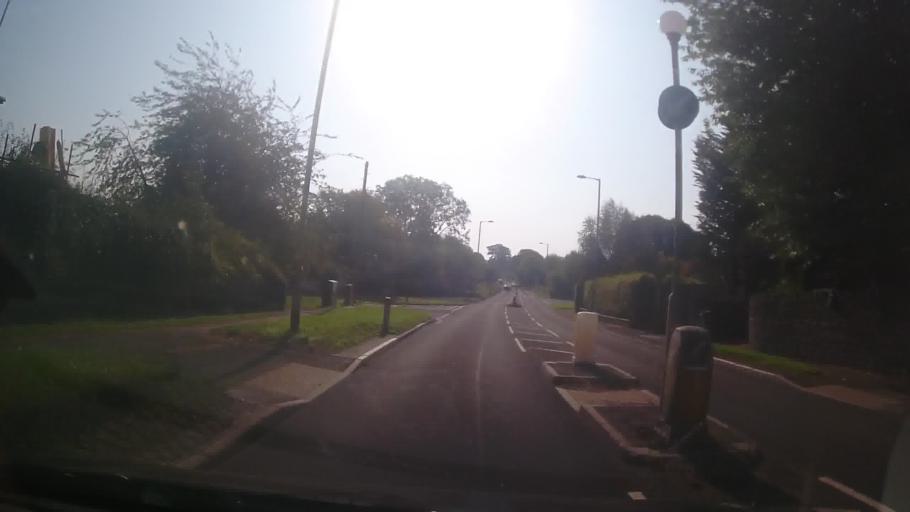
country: GB
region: England
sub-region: Shropshire
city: Much Wenlock
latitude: 52.5920
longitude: -2.5569
